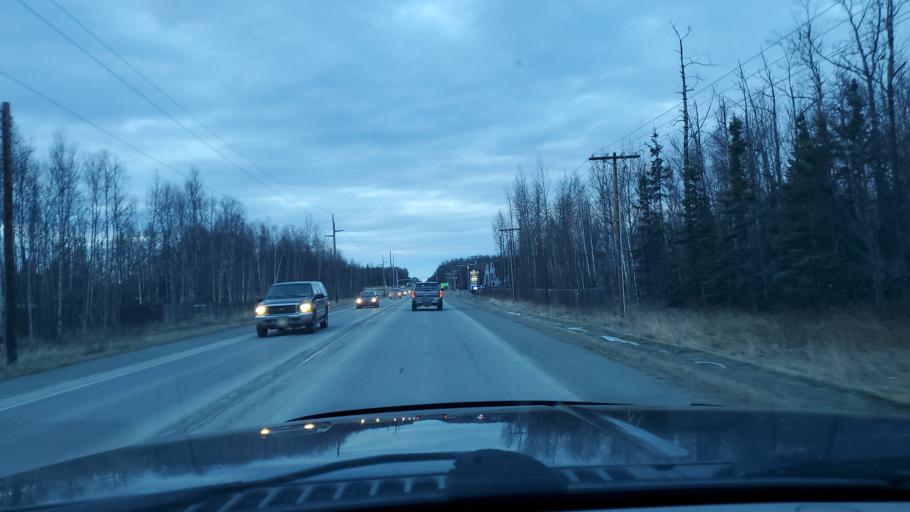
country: US
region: Alaska
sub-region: Matanuska-Susitna Borough
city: Lakes
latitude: 61.6139
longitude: -149.3228
